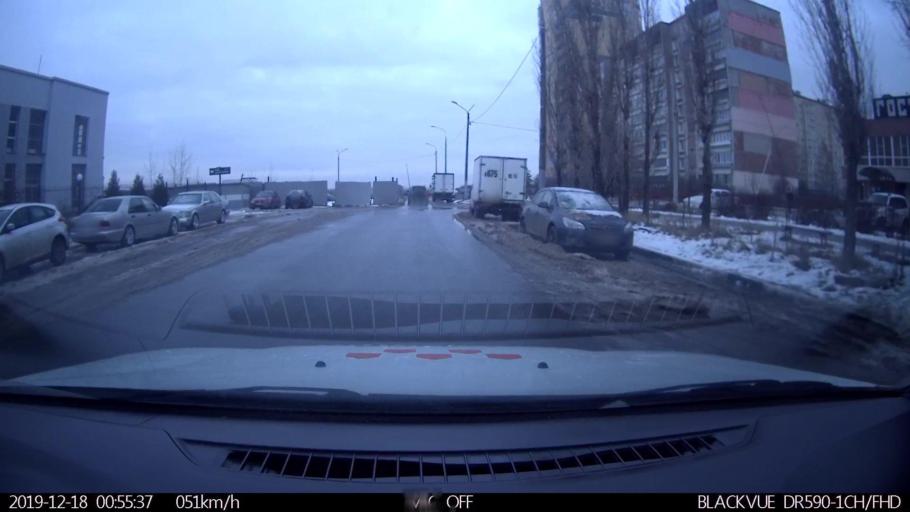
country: RU
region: Nizjnij Novgorod
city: Nizhniy Novgorod
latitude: 56.3487
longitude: 43.9271
